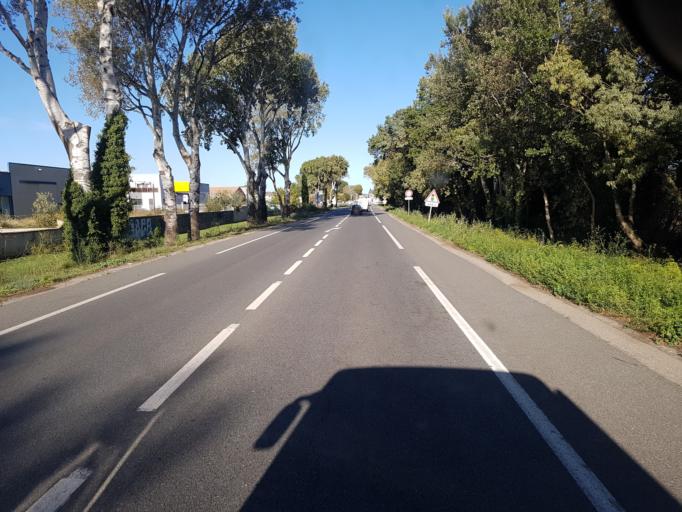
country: FR
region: Languedoc-Roussillon
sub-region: Departement de l'Aude
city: Coursan
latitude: 43.2260
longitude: 3.0476
